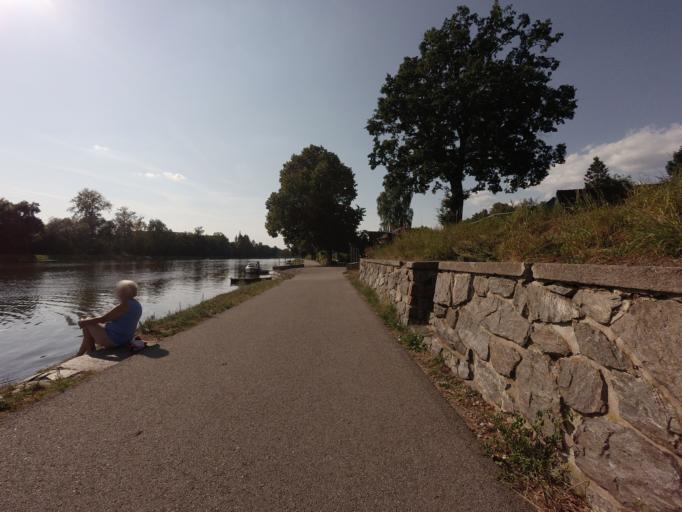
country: CZ
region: Jihocesky
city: Tyn nad Vltavou
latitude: 49.2172
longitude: 14.4325
